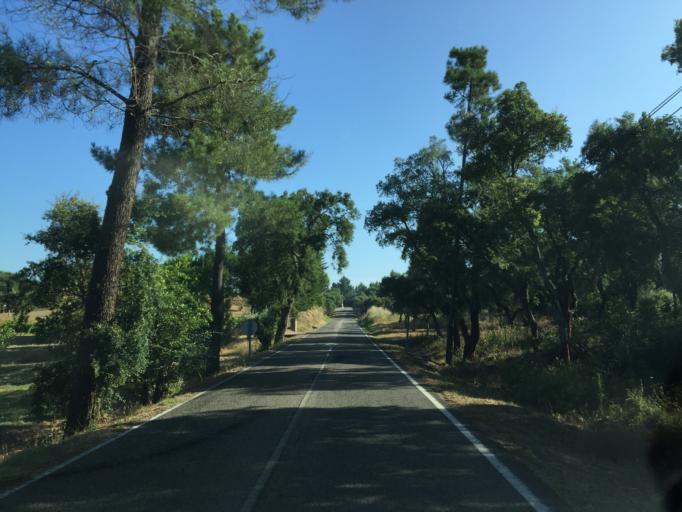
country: PT
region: Santarem
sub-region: Abrantes
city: Alferrarede
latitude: 39.5302
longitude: -8.1378
